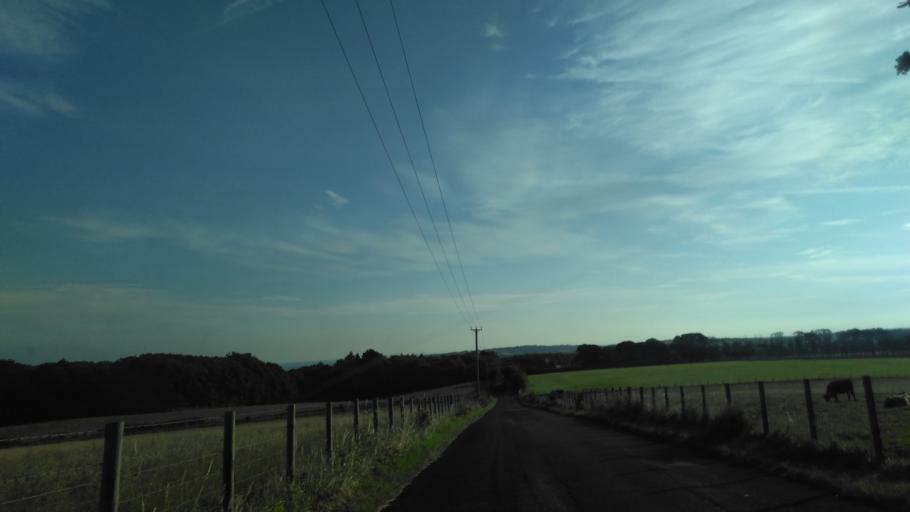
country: GB
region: England
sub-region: Kent
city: Dunkirk
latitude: 51.3011
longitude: 0.9851
